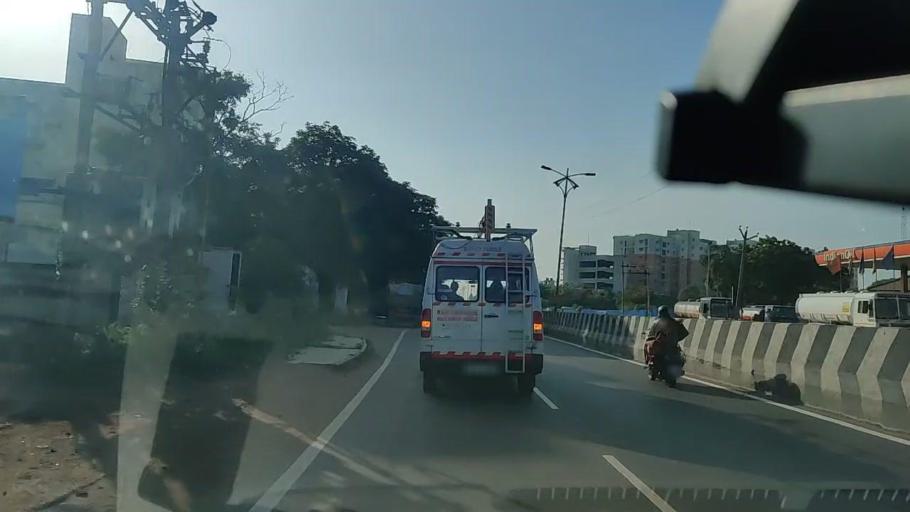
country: IN
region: Tamil Nadu
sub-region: Thiruvallur
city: Chinnasekkadu
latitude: 13.1410
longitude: 80.2252
